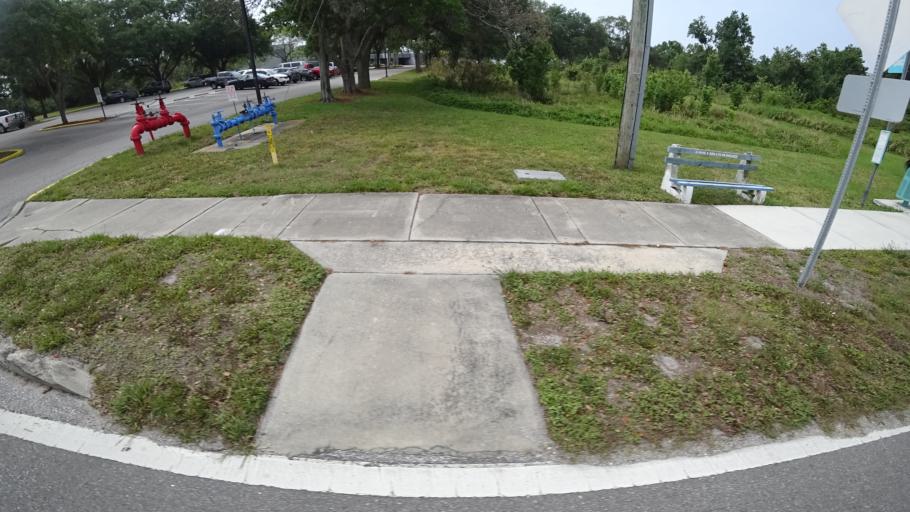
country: US
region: Florida
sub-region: Manatee County
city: West Samoset
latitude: 27.4669
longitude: -82.5500
